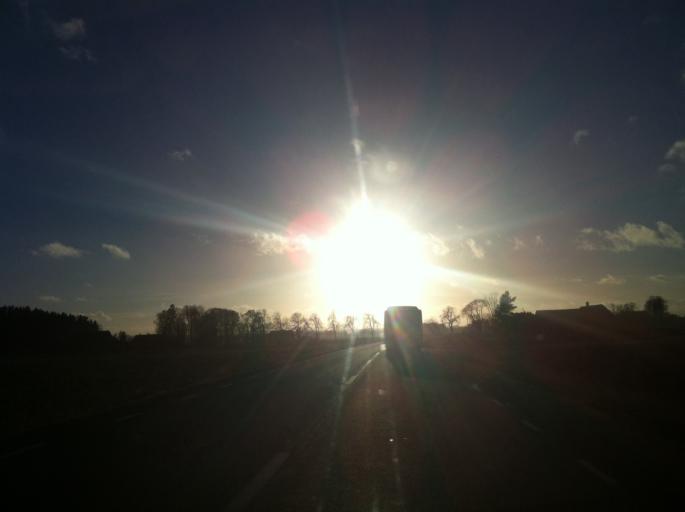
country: SE
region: Skane
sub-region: Hassleholms Kommun
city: Hastveda
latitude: 56.1944
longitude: 13.9345
